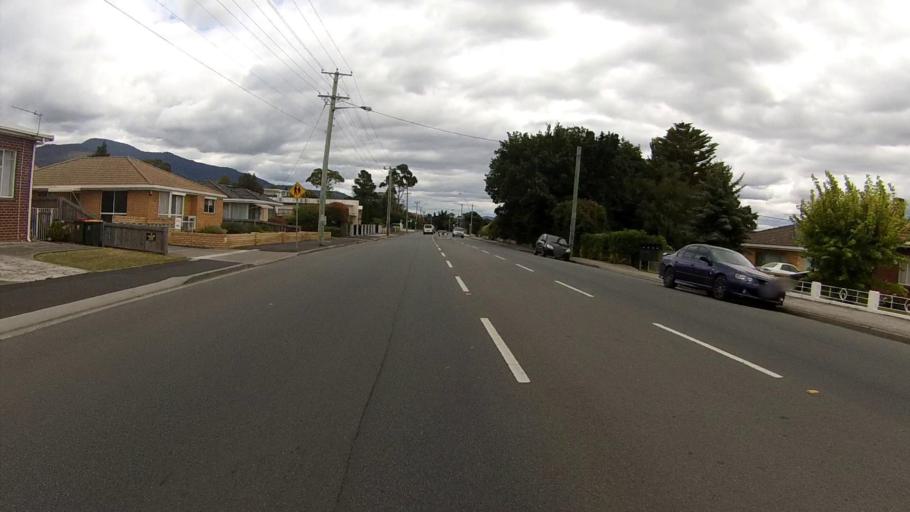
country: AU
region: Tasmania
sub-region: Glenorchy
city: Glenorchy
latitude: -42.8238
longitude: 147.2647
